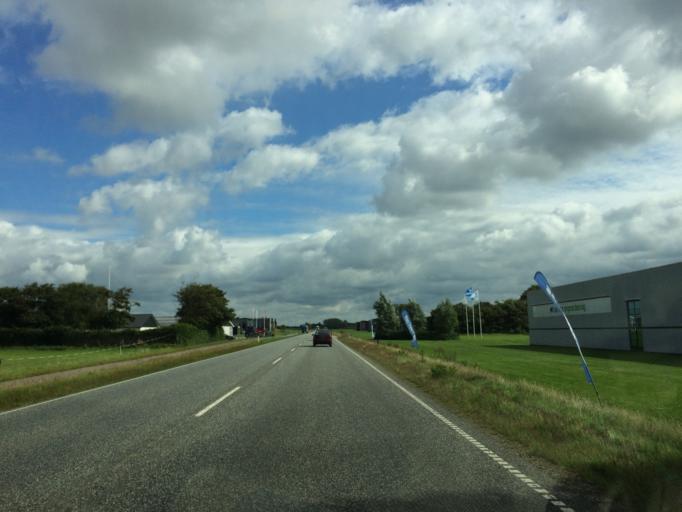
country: DK
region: Central Jutland
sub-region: Holstebro Kommune
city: Holstebro
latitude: 56.3621
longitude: 8.6600
